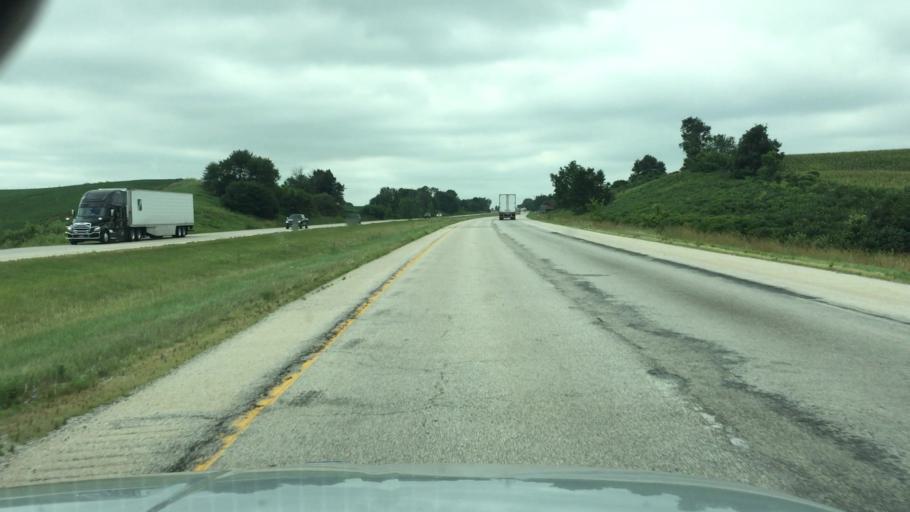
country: US
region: Illinois
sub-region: Henry County
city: Orion
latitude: 41.2484
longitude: -90.3302
